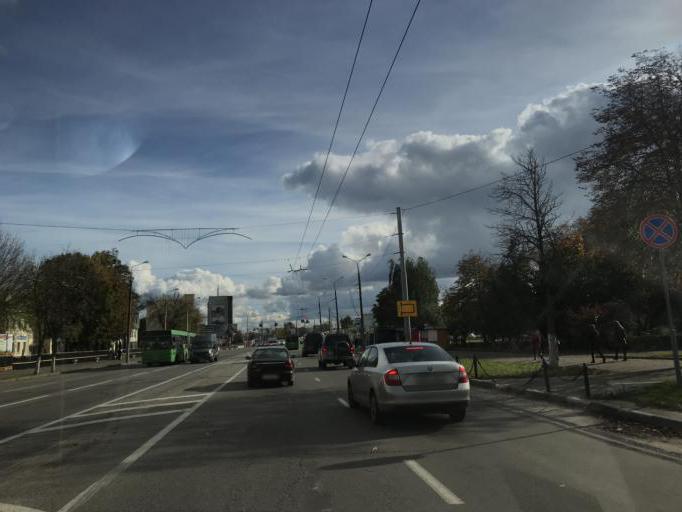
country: BY
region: Gomel
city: Gomel
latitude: 52.4485
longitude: 30.9689
